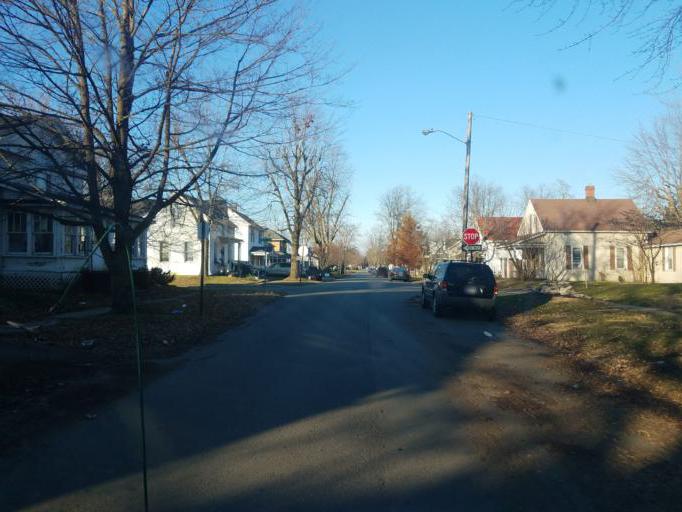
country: US
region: Ohio
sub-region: Hardin County
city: Kenton
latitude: 40.6520
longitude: -83.6054
